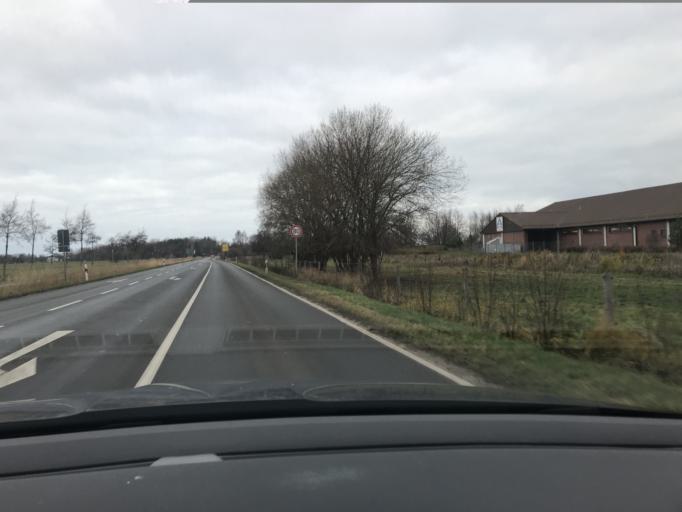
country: DE
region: Mecklenburg-Vorpommern
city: Ostseebad Dierhagen
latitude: 54.2925
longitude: 12.3528
